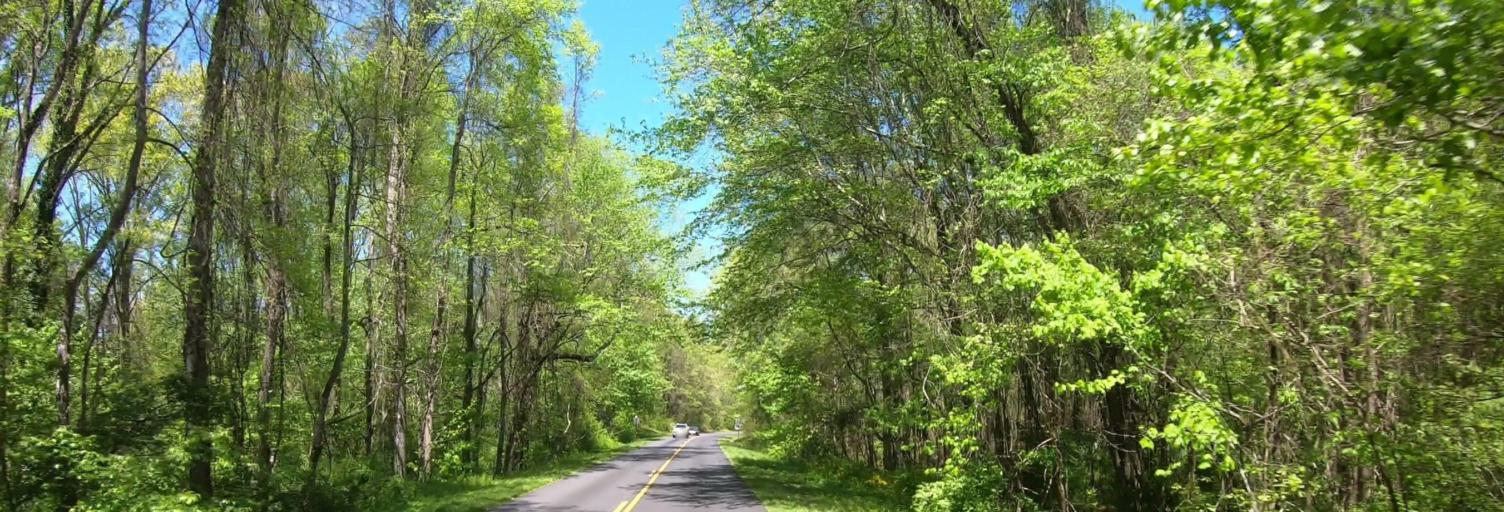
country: US
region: North Carolina
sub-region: Buncombe County
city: Biltmore Forest
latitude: 35.5583
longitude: -82.4957
